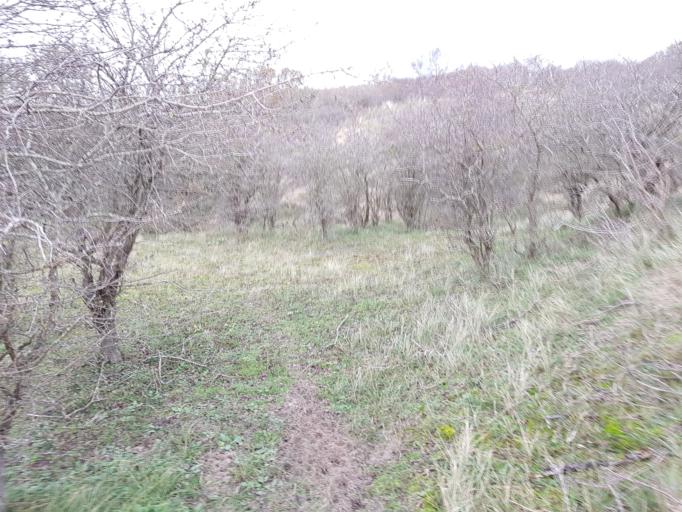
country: NL
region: South Holland
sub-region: Gemeente Noordwijkerhout
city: Noordwijkerhout
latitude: 52.3022
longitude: 4.5007
